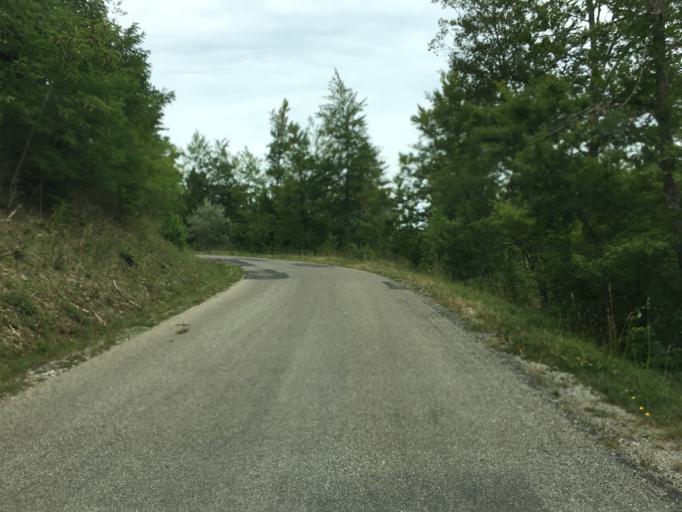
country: FR
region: Provence-Alpes-Cote d'Azur
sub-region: Departement des Alpes-de-Haute-Provence
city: Digne-les-Bains
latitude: 44.2271
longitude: 6.1340
